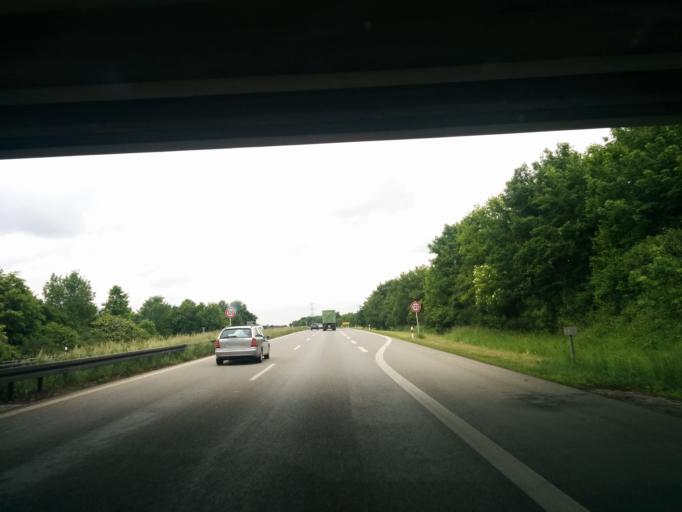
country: DE
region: Bavaria
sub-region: Swabia
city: Oberottmarshausen
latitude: 48.2223
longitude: 10.8650
